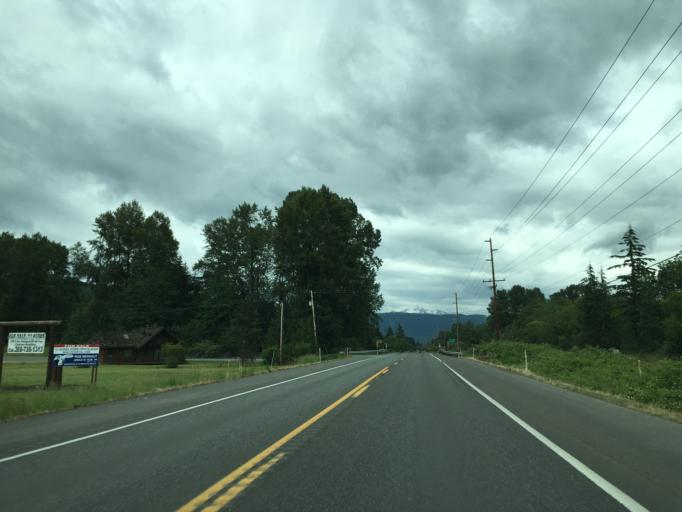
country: US
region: Washington
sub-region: Whatcom County
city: Nooksack
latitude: 48.8421
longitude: -122.2620
